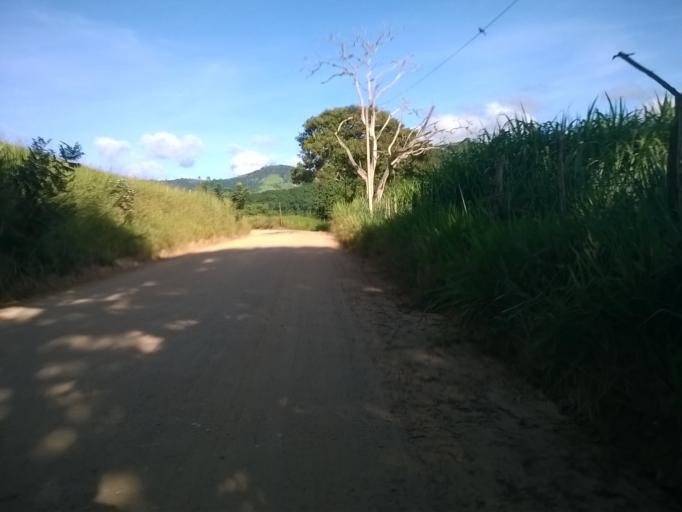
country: BR
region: Minas Gerais
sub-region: Uba
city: Uba
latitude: -21.0813
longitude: -42.9930
